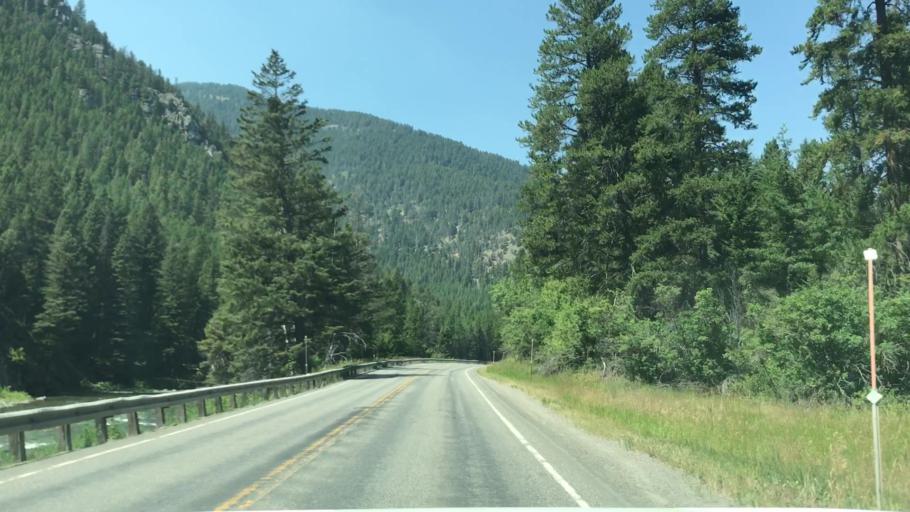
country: US
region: Montana
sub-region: Gallatin County
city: Big Sky
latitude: 45.3979
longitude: -111.2134
